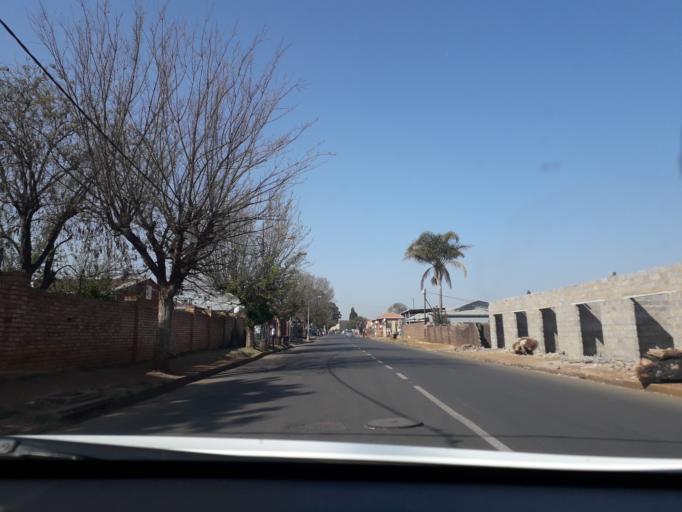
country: ZA
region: Gauteng
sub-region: City of Johannesburg Metropolitan Municipality
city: Modderfontein
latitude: -26.1027
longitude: 28.2387
